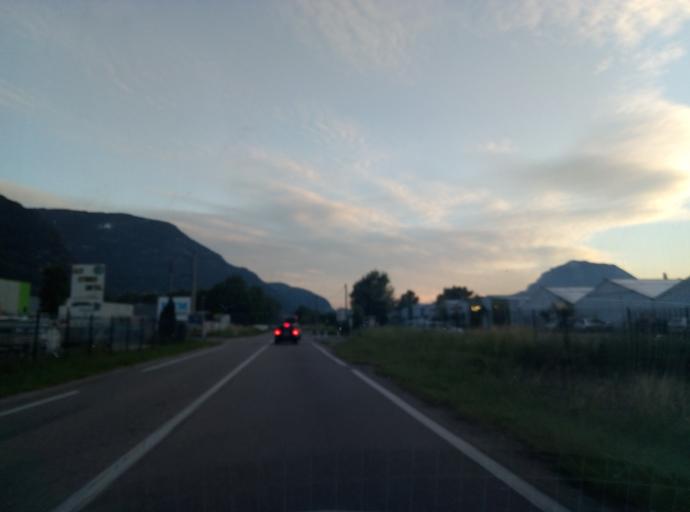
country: FR
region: Rhone-Alpes
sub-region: Departement de l'Isere
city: Noyarey
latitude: 45.2557
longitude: 5.6284
